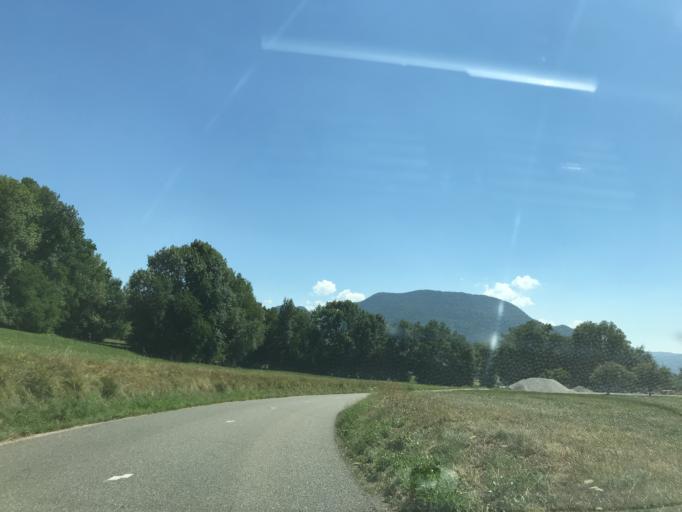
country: FR
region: Rhone-Alpes
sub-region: Departement de la Haute-Savoie
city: Villaz
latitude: 45.9451
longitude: 6.1948
